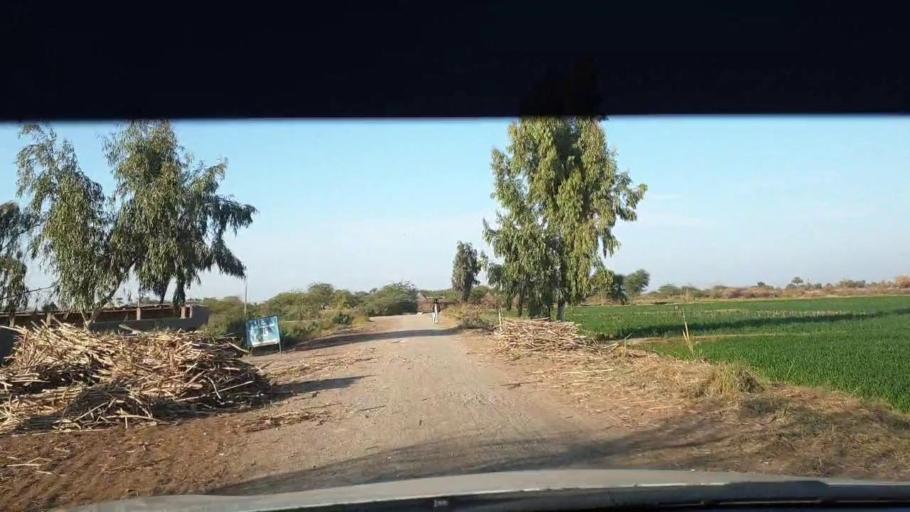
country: PK
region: Sindh
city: Berani
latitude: 25.8216
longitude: 68.9097
